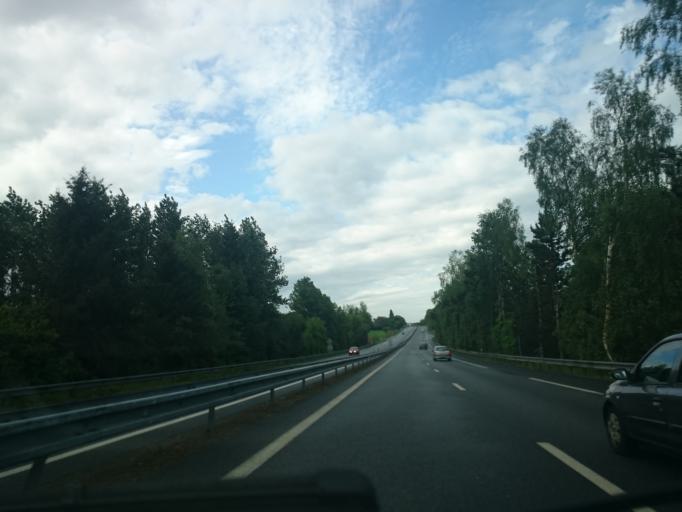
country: FR
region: Brittany
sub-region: Departement du Morbihan
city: Ploermel
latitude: 47.8932
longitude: -2.4136
